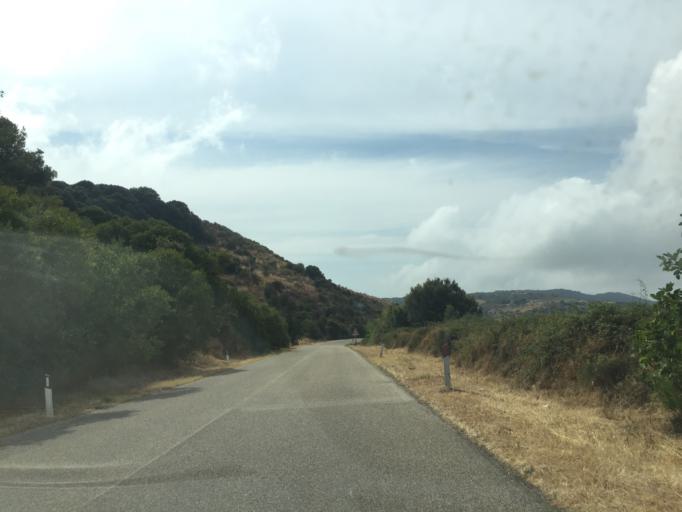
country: IT
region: Sardinia
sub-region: Provincia di Olbia-Tempio
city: Trinita d'Agultu
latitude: 40.9750
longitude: 8.9484
